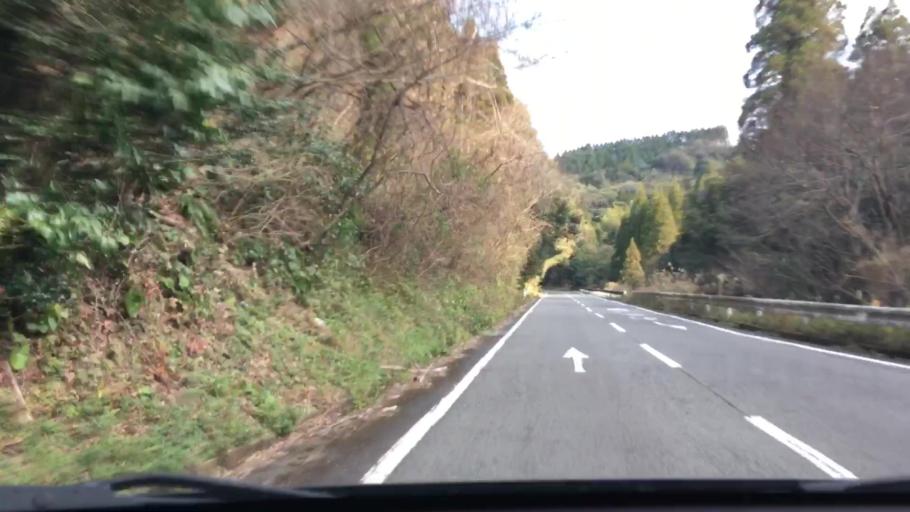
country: JP
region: Miyazaki
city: Nichinan
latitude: 31.5911
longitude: 131.3030
